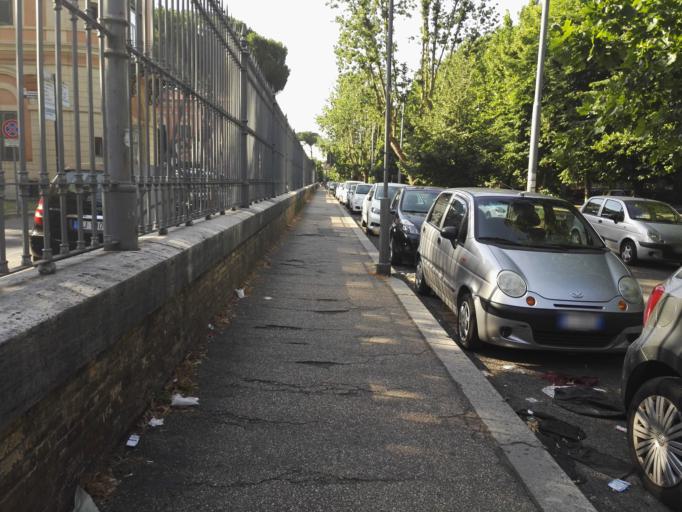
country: IT
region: Latium
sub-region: Citta metropolitana di Roma Capitale
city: Rome
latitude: 41.9058
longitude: 12.5100
